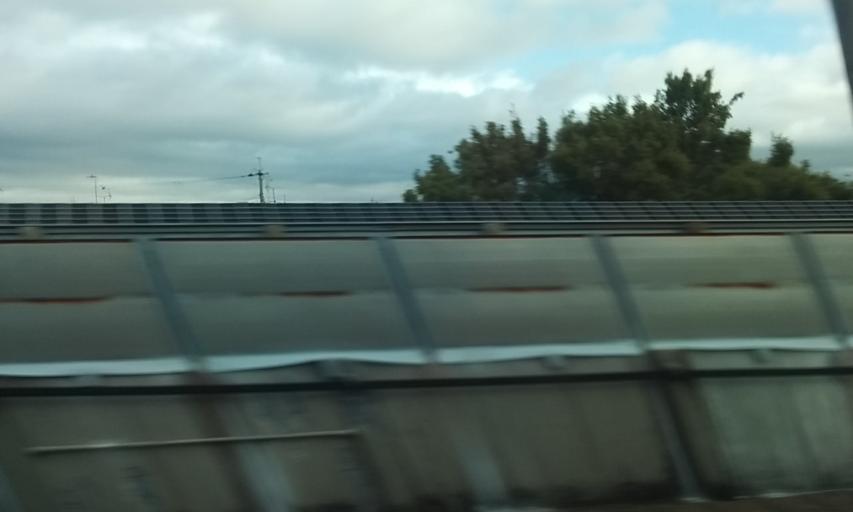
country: JP
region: Hyogo
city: Akashi
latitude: 34.6660
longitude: 134.9733
